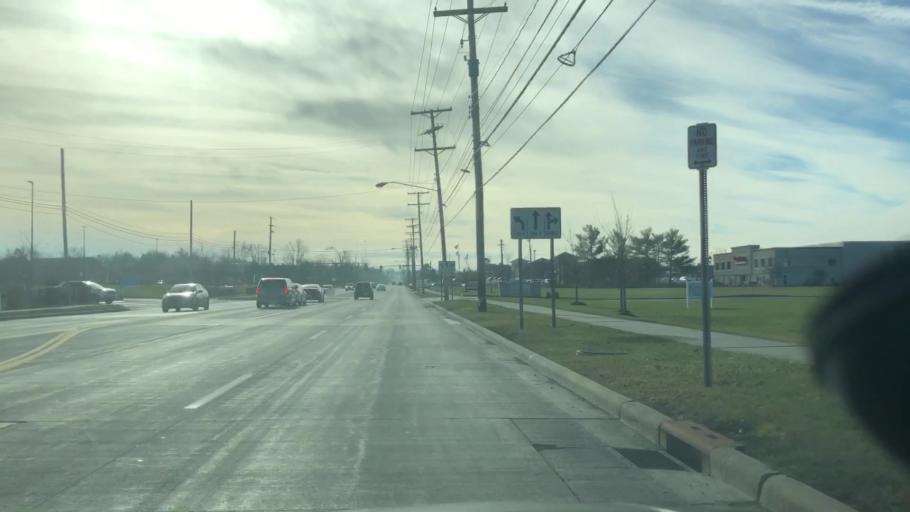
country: US
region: Ohio
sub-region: Cuyahoga County
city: Strongsville
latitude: 41.3019
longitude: -81.8353
